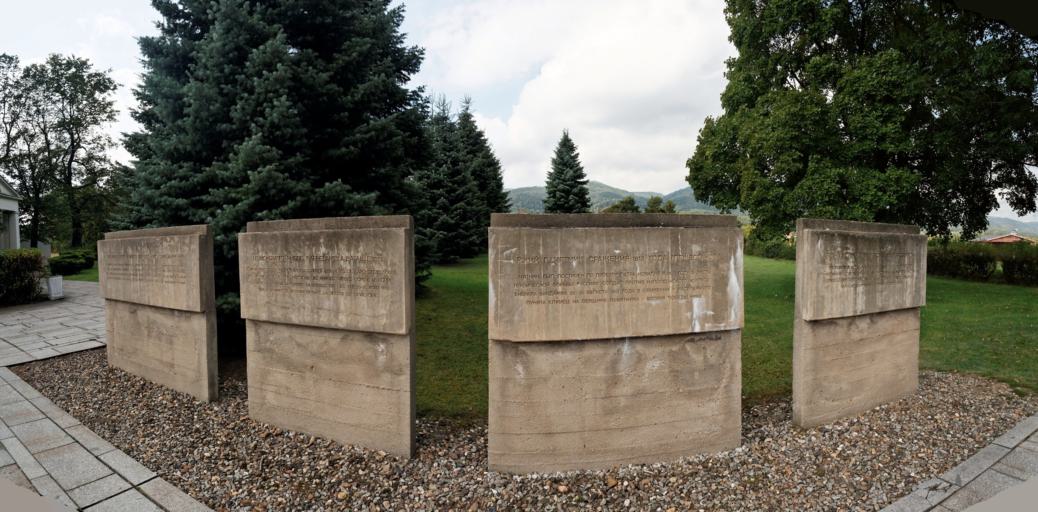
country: CZ
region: Ustecky
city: Chabarovice
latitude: 50.6825
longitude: 13.9142
